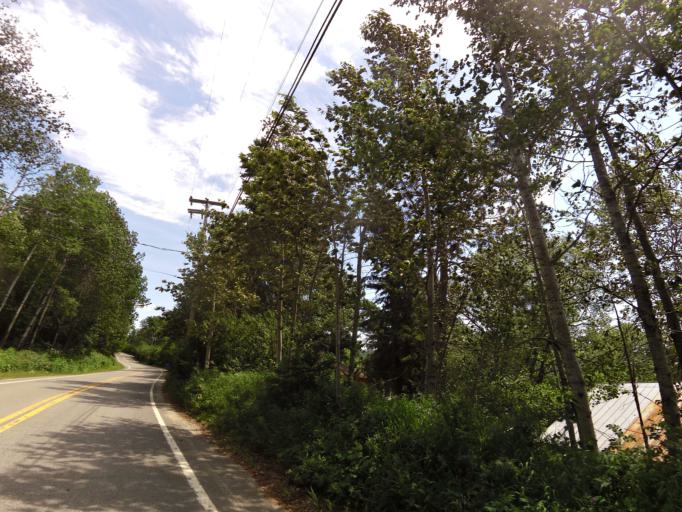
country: CA
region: Quebec
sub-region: Abitibi-Temiscamingue
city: Ville-Marie
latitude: 47.2909
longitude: -79.4517
